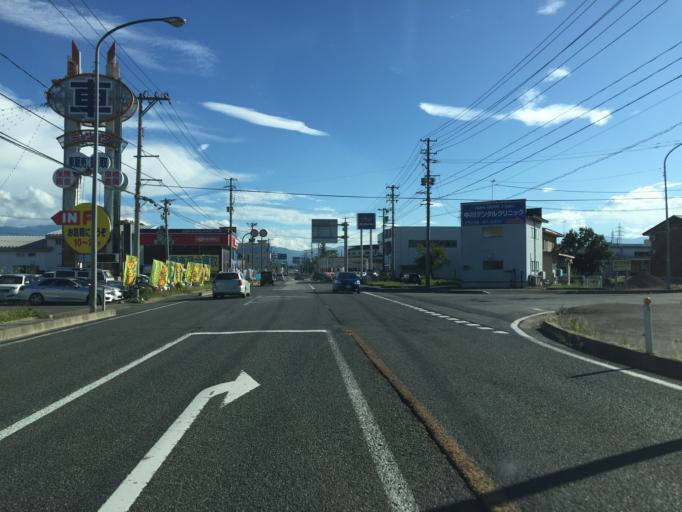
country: JP
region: Yamagata
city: Yonezawa
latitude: 37.9506
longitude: 140.1233
